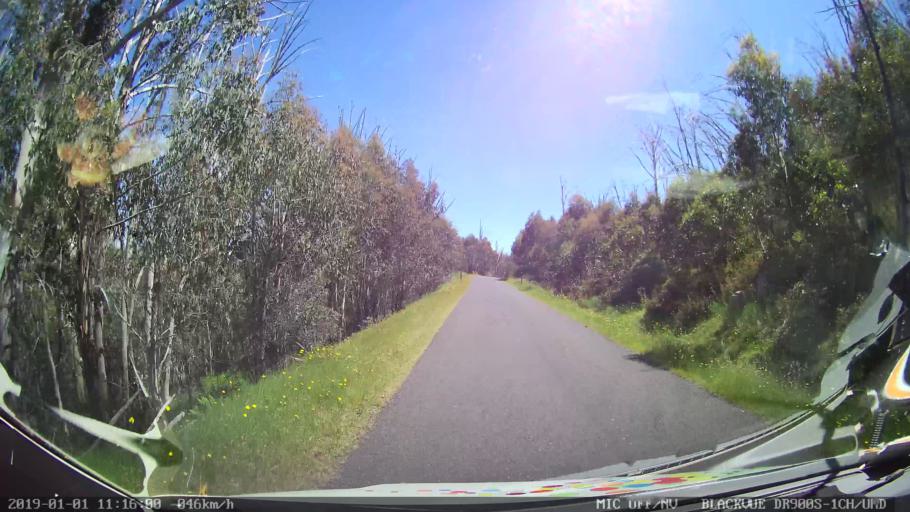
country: AU
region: New South Wales
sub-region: Snowy River
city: Jindabyne
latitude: -35.9417
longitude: 148.3857
